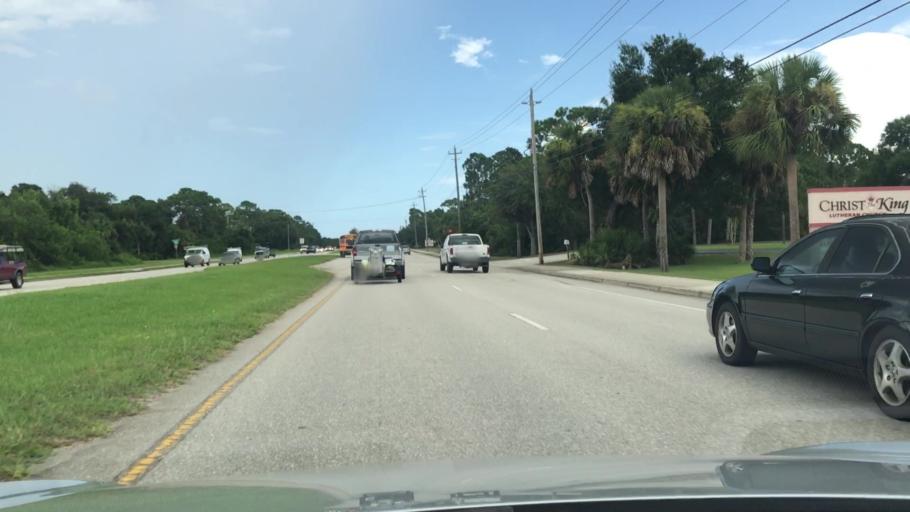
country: US
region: Florida
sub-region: Indian River County
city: Sebastian
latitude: 27.7714
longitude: -80.5040
